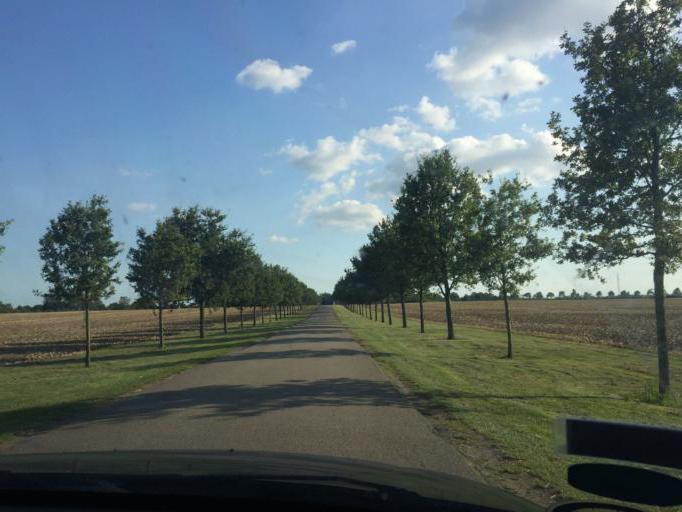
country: DK
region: Zealand
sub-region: Lolland Kommune
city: Maribo
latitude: 54.8045
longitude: 11.5084
